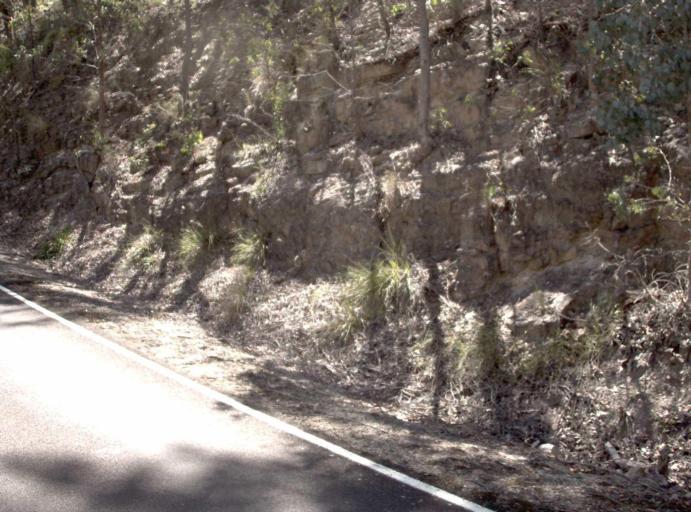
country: AU
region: Victoria
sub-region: East Gippsland
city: Lakes Entrance
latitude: -37.3815
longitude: 148.2187
